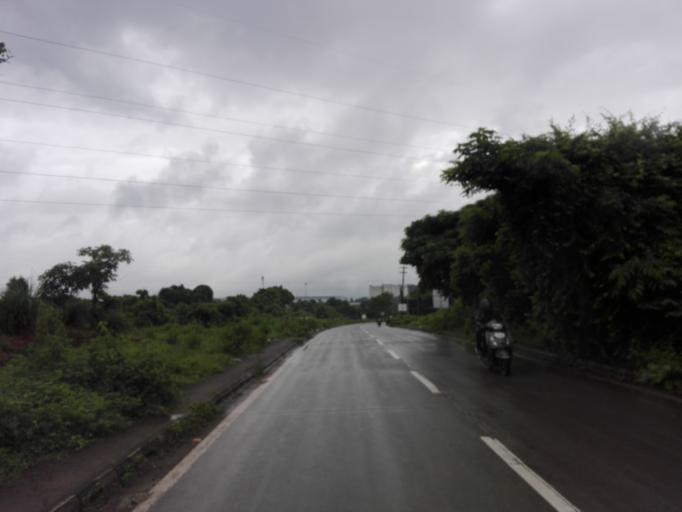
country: IN
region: Kerala
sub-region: Ernakulam
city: Aluva
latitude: 10.0509
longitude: 76.3470
